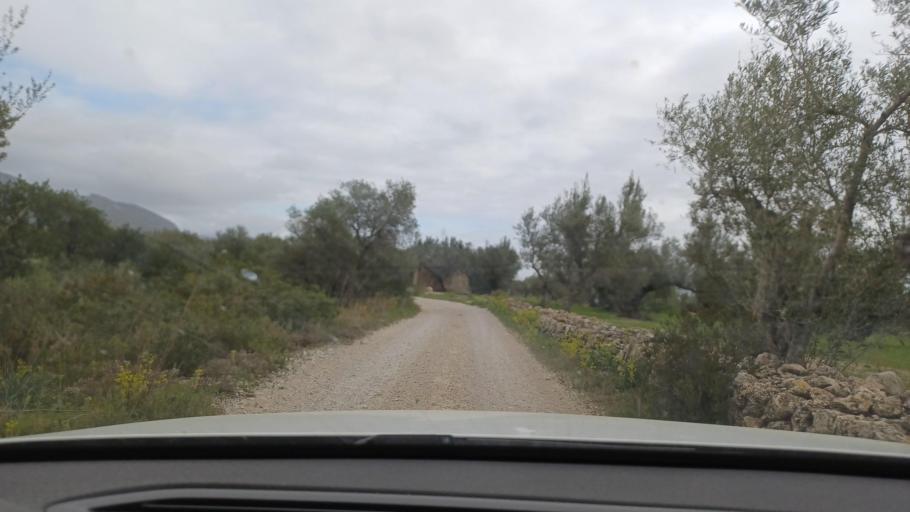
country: ES
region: Catalonia
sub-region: Provincia de Tarragona
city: Mas de Barberans
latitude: 40.8004
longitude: 0.4168
